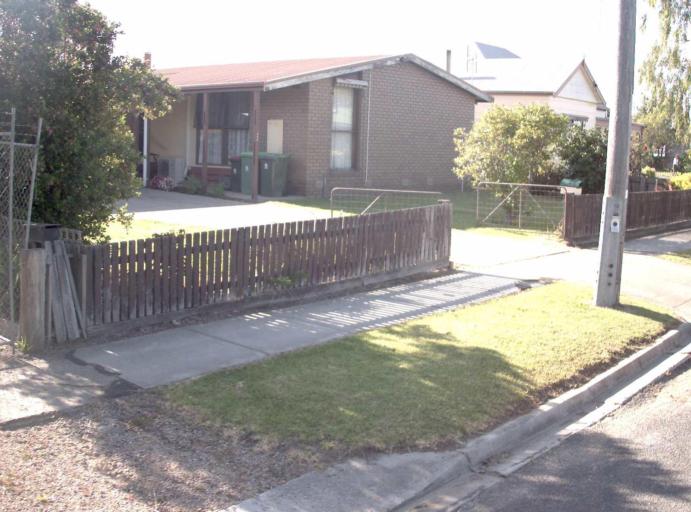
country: AU
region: Victoria
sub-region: East Gippsland
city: Lakes Entrance
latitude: -37.6961
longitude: 148.4576
